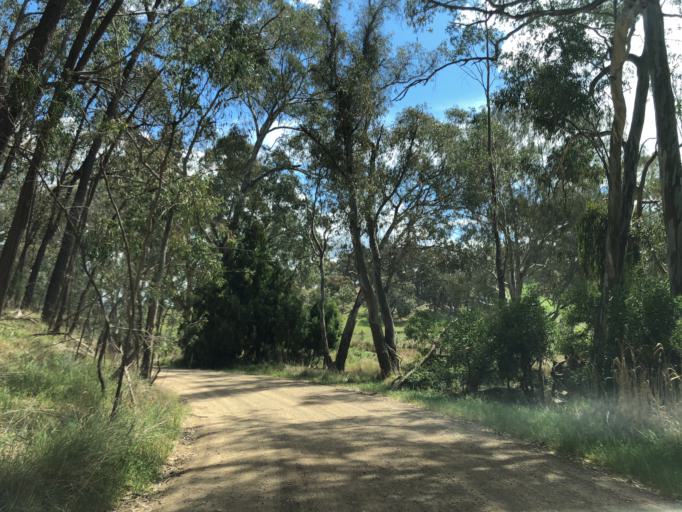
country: AU
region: Victoria
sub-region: Benalla
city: Benalla
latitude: -36.7308
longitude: 146.1348
